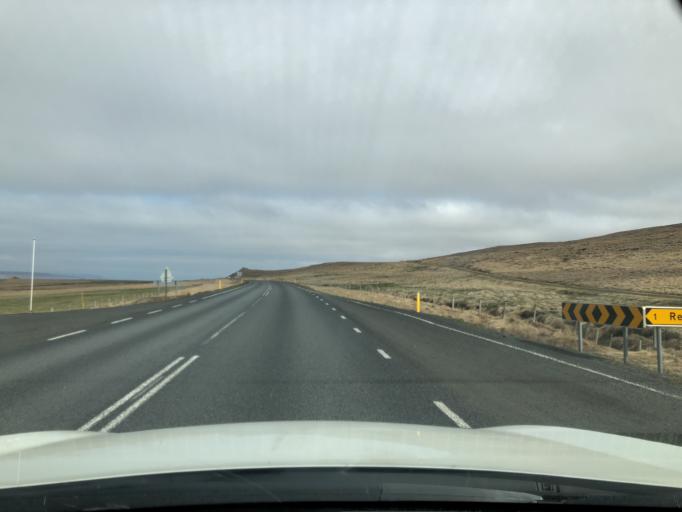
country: IS
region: West
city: Borgarnes
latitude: 65.2508
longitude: -21.0882
